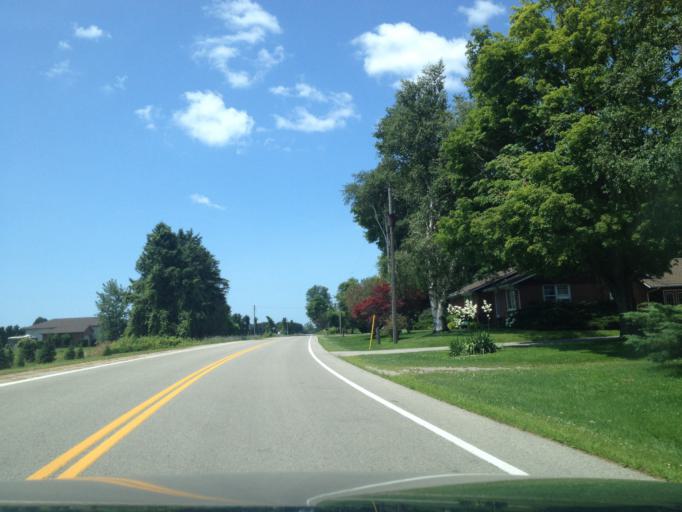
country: CA
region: Ontario
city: Norfolk County
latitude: 42.5942
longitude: -80.4864
